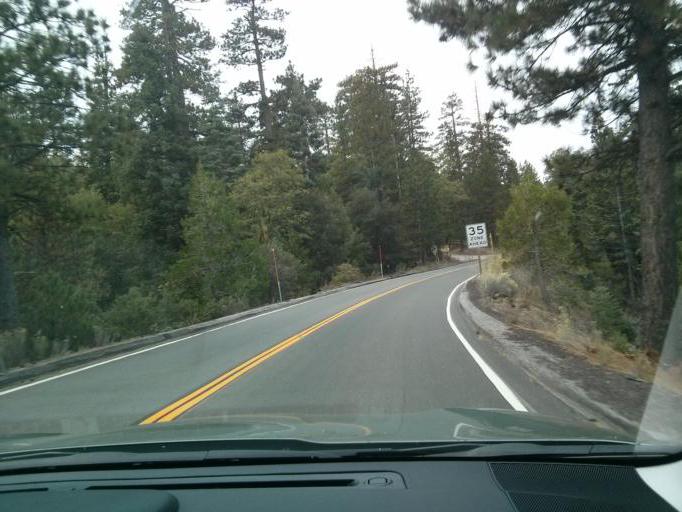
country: US
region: California
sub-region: San Bernardino County
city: Big Bear Lake
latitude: 34.1519
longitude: -116.9739
